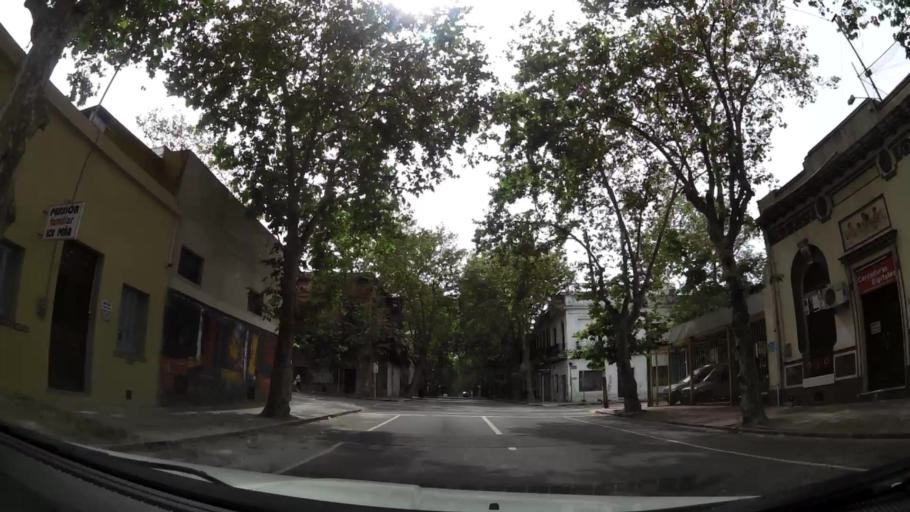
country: UY
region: Montevideo
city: Montevideo
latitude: -34.9096
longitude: -56.1891
